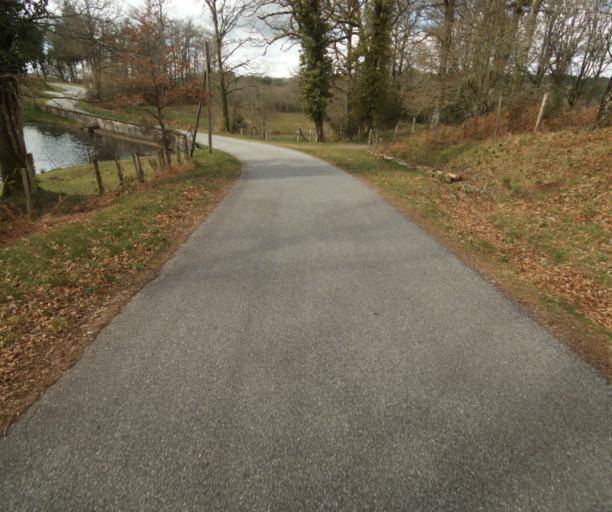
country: FR
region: Limousin
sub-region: Departement de la Correze
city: Correze
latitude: 45.3872
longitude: 1.8955
